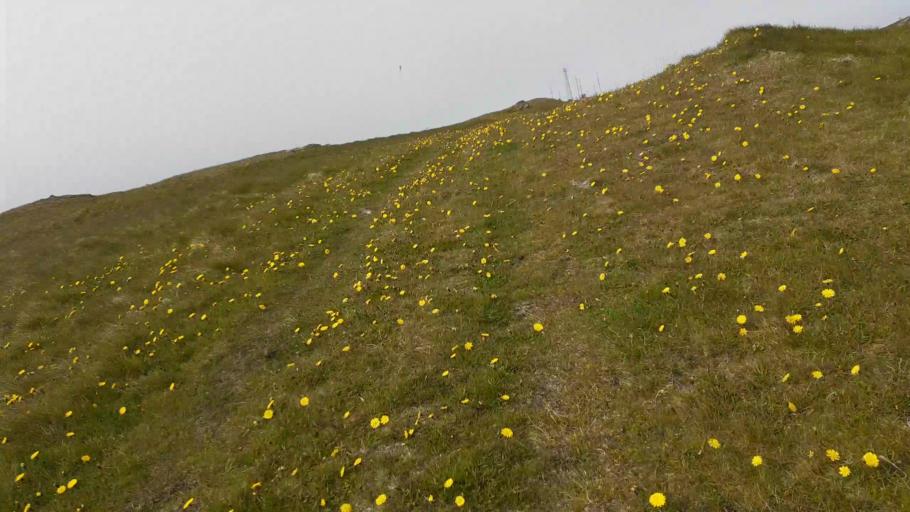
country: IS
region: Northeast
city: Dalvik
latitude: 66.5418
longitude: -17.9917
